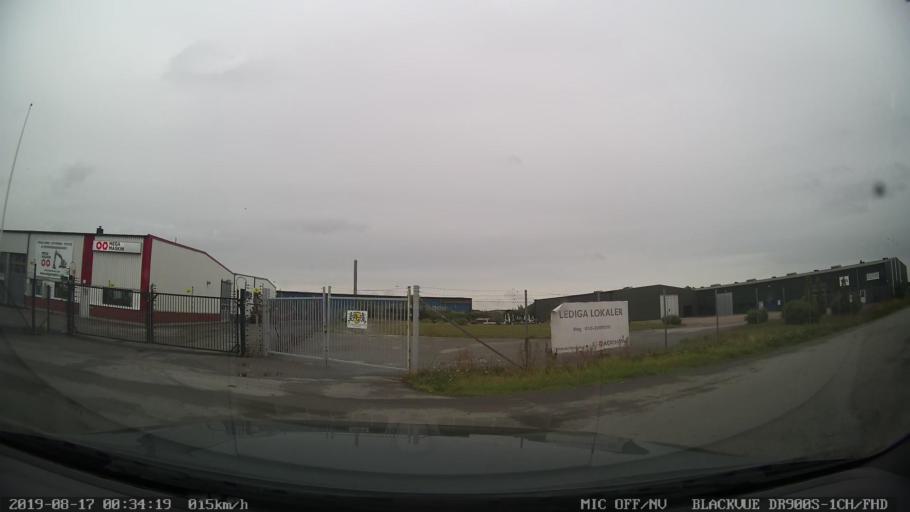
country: SE
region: Skane
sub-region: Landskrona
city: Landskrona
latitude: 55.8591
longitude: 12.8388
